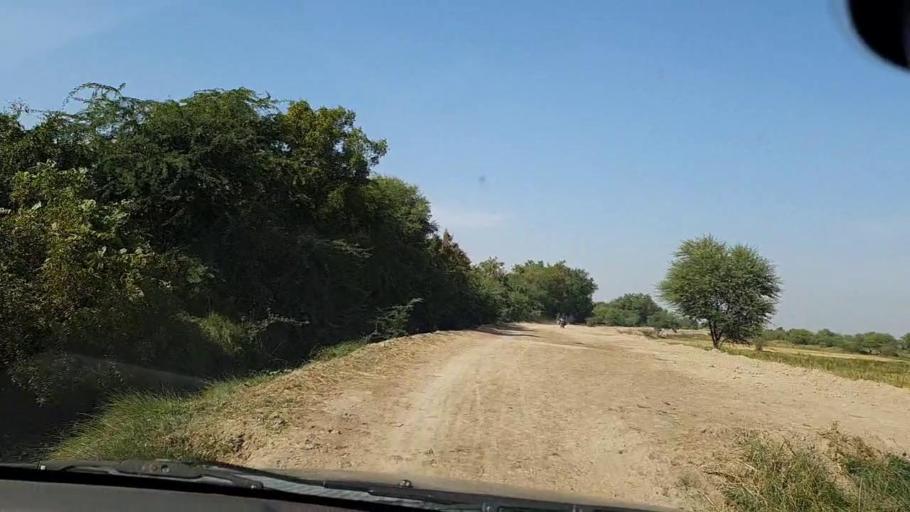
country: PK
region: Sindh
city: Mirpur Batoro
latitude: 24.6543
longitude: 68.2538
